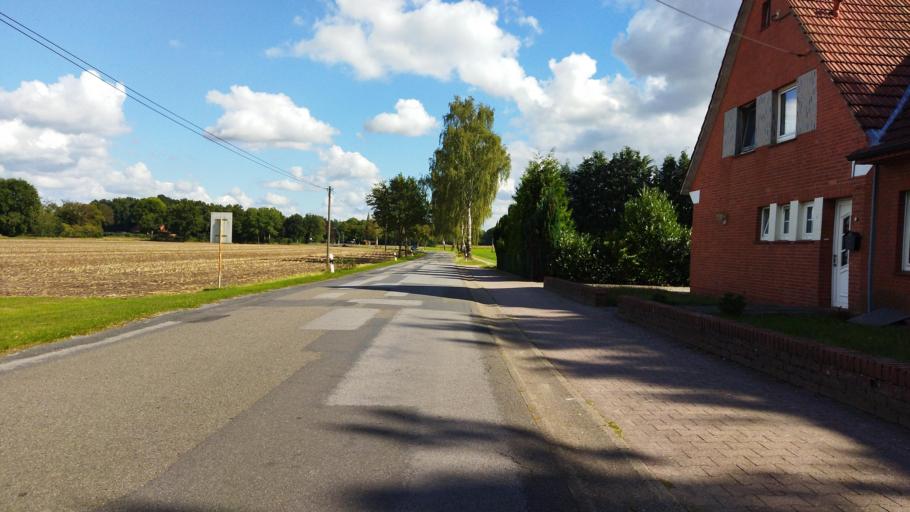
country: DE
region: Lower Saxony
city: Lingen
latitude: 52.4550
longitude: 7.3546
